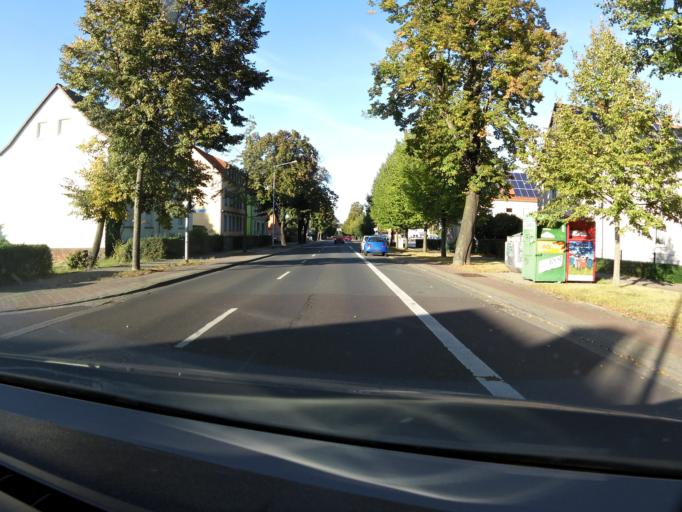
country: DE
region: Saxony-Anhalt
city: Diesdorf
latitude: 52.0937
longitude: 11.5718
